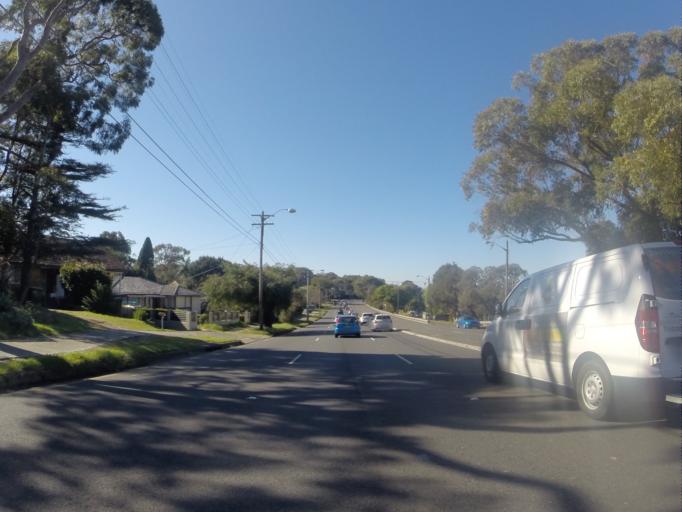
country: AU
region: New South Wales
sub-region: Sutherland Shire
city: Kareela
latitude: -34.0095
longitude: 151.0980
